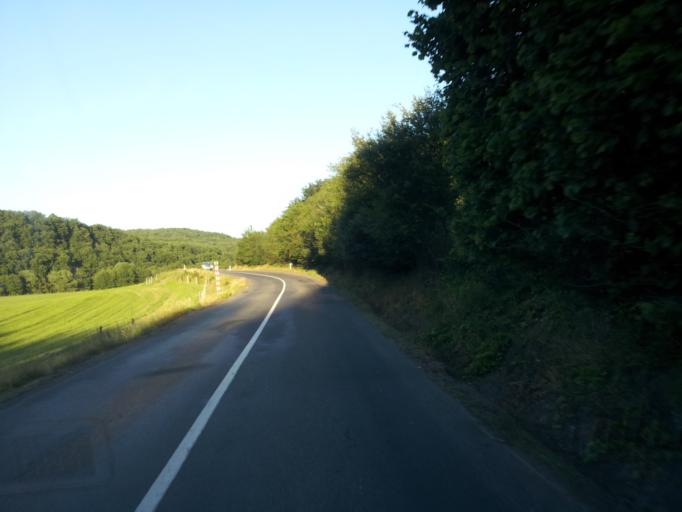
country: SK
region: Banskobystricky
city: Svaety Anton
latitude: 48.3423
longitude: 18.9437
